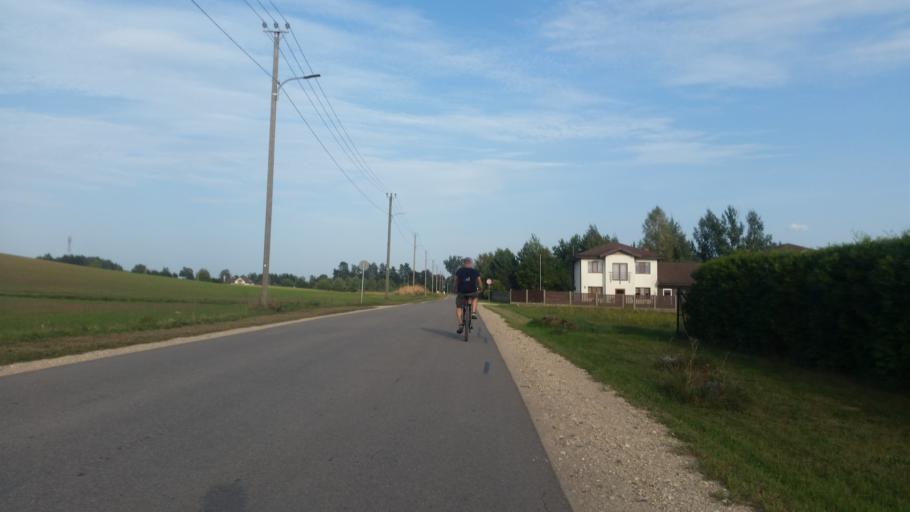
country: LV
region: Ikskile
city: Ikskile
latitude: 56.8183
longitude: 24.5205
